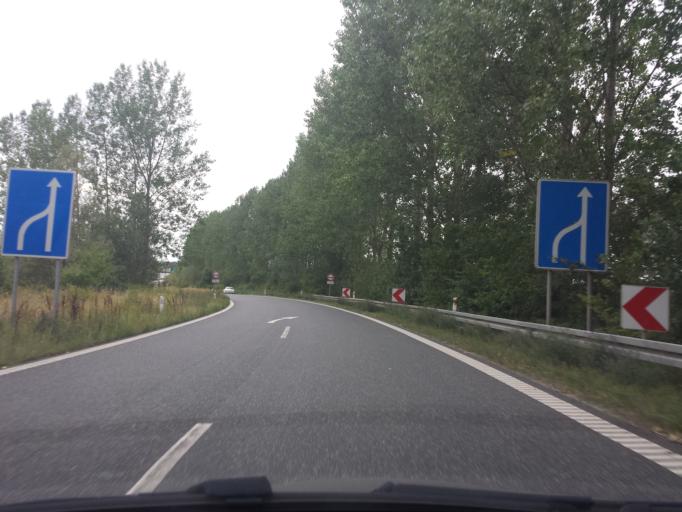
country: DK
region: Capital Region
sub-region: Hoje-Taastrup Kommune
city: Flong
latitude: 55.6556
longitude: 12.2066
